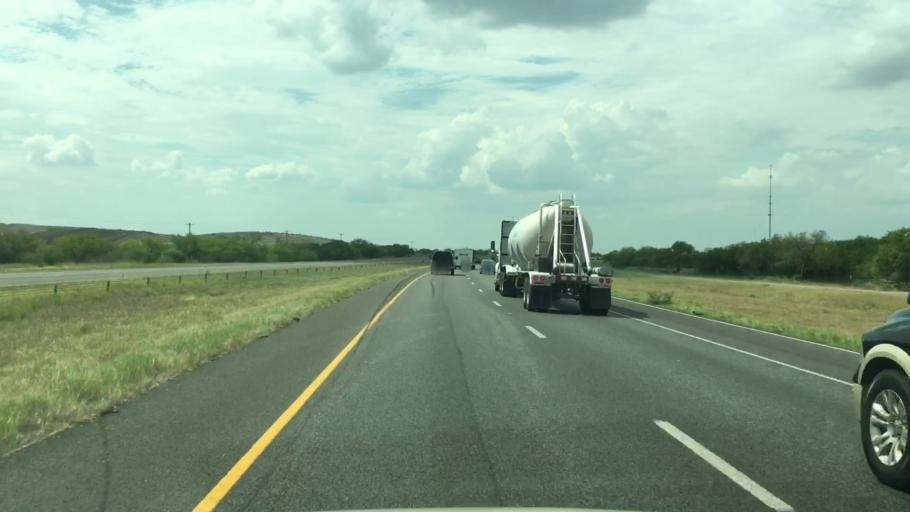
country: US
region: Texas
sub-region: Atascosa County
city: Pleasanton
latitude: 28.7884
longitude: -98.3278
